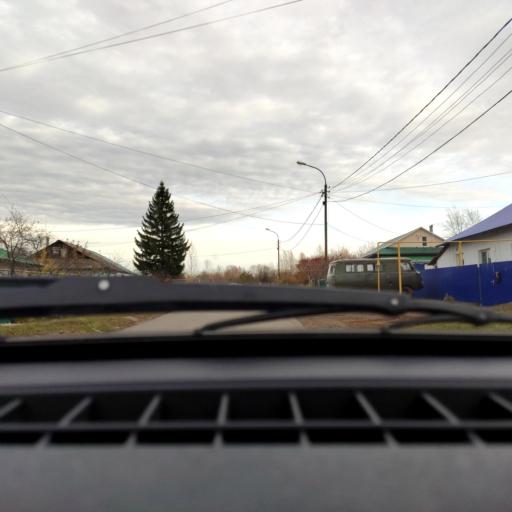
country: RU
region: Bashkortostan
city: Blagoveshchensk
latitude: 54.9012
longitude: 56.1509
